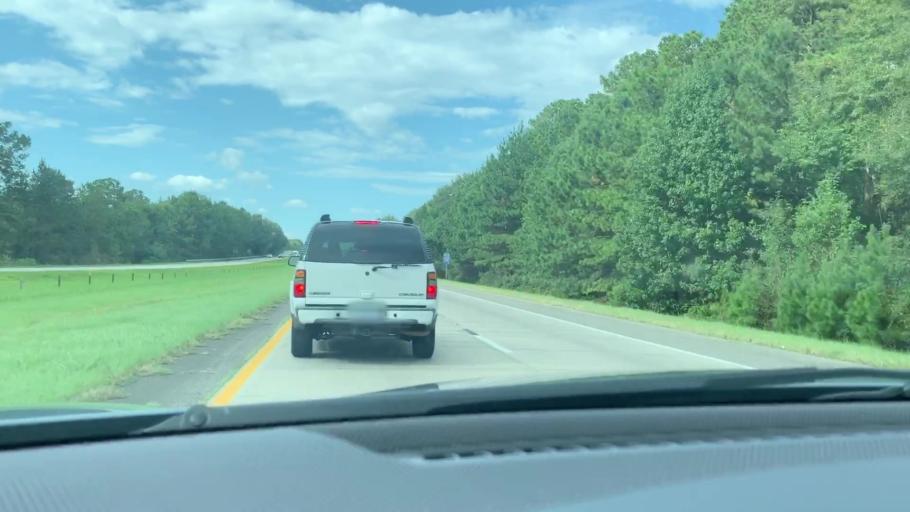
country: US
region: South Carolina
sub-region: Hampton County
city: Yemassee
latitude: 32.6389
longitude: -80.8825
